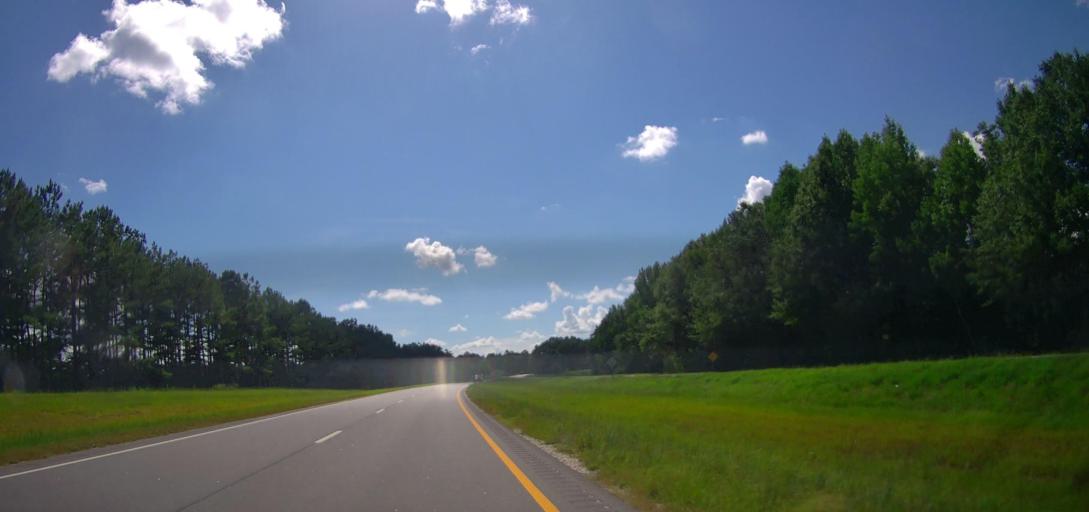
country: US
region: Alabama
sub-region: Macon County
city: Tuskegee
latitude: 32.3783
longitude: -85.7802
